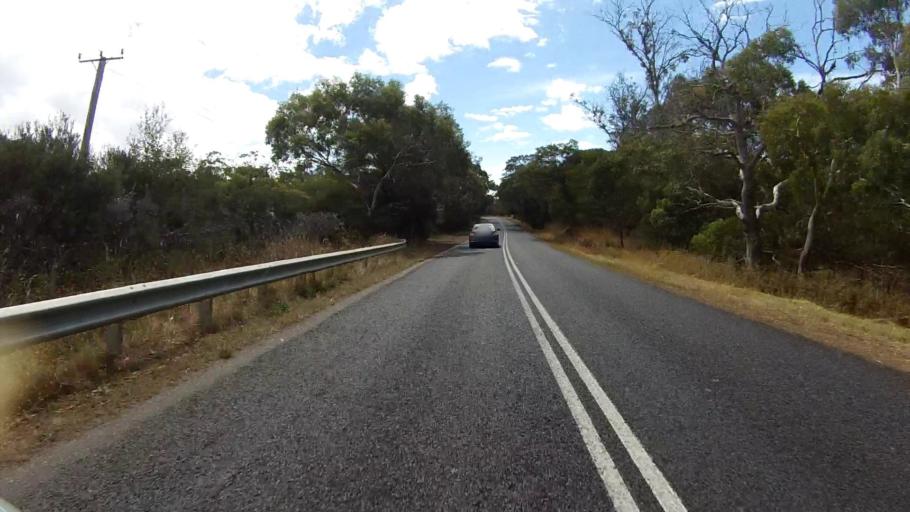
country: AU
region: Tasmania
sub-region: Sorell
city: Sorell
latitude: -42.1522
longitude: 148.0683
